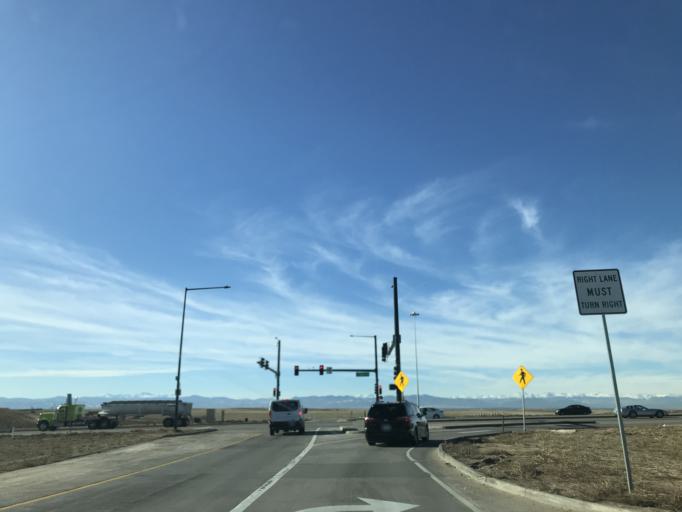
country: US
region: Colorado
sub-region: Adams County
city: Aurora
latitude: 39.8349
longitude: -104.7711
